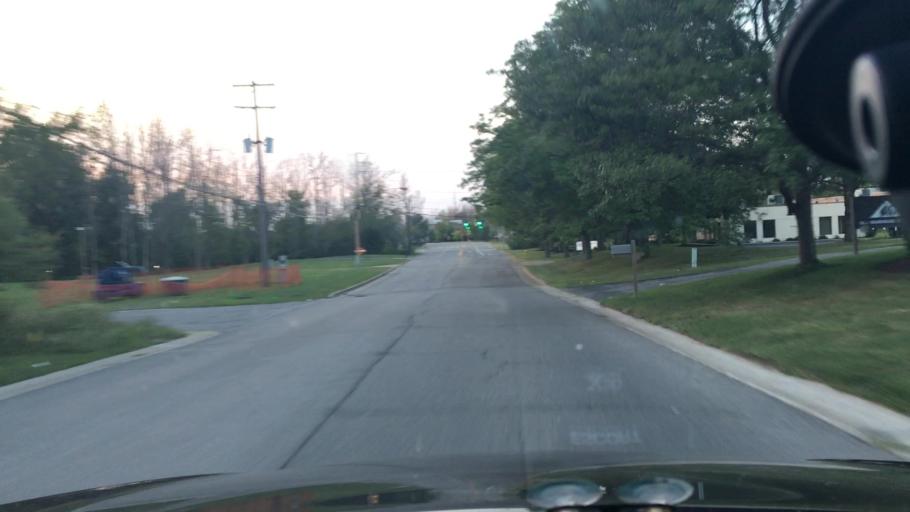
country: US
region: New York
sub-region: Erie County
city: Orchard Park
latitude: 42.7870
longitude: -78.7665
